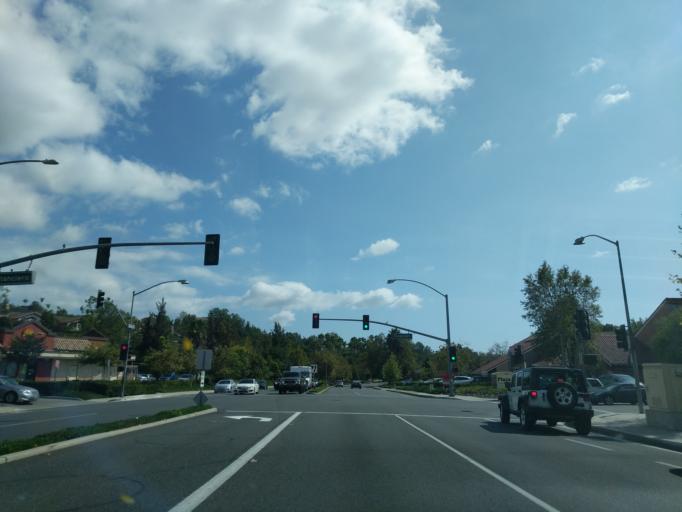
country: US
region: California
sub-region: Orange County
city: Mission Viejo
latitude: 33.5920
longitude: -117.6600
